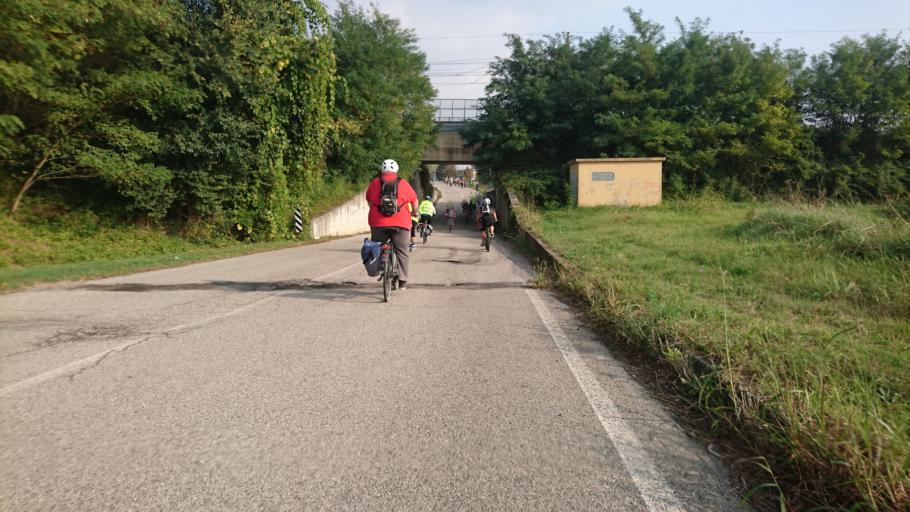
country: IT
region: Veneto
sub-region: Provincia di Rovigo
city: Arqua Polesine
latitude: 44.9972
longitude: 11.7425
